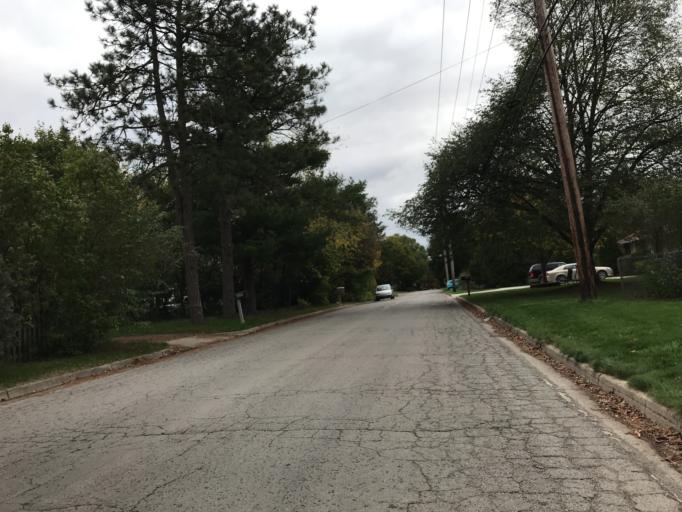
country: US
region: Michigan
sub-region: Washtenaw County
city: Ann Arbor
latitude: 42.2540
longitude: -83.7287
